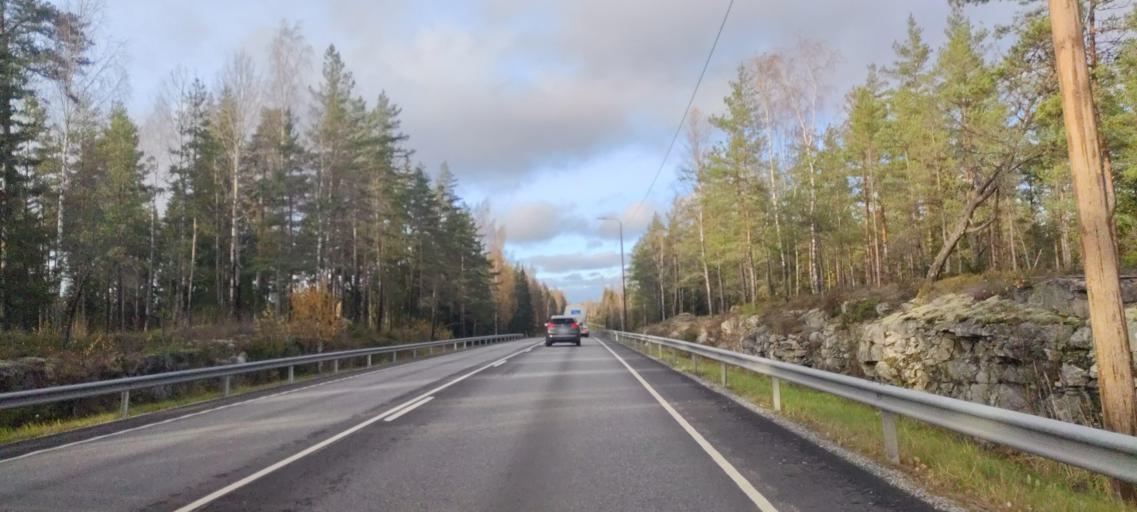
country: FI
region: Varsinais-Suomi
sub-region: Turku
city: Mynaemaeki
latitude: 60.7714
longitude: 21.8930
